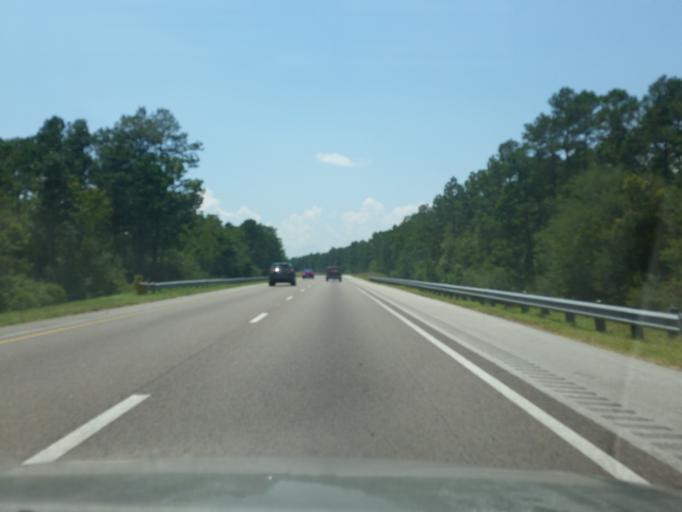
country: US
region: Florida
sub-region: Escambia County
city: Cantonment
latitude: 30.5784
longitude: -87.4359
